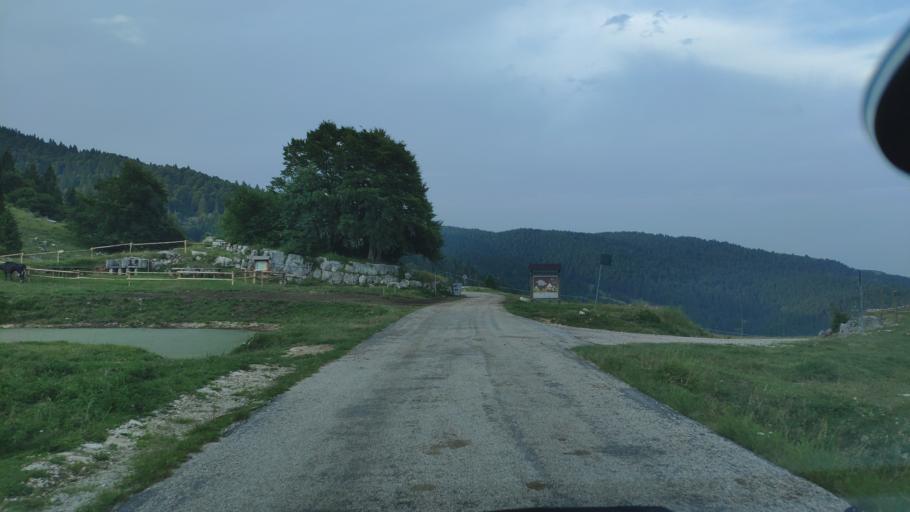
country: IT
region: Veneto
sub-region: Provincia di Vicenza
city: Calvene
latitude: 45.7937
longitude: 11.4917
